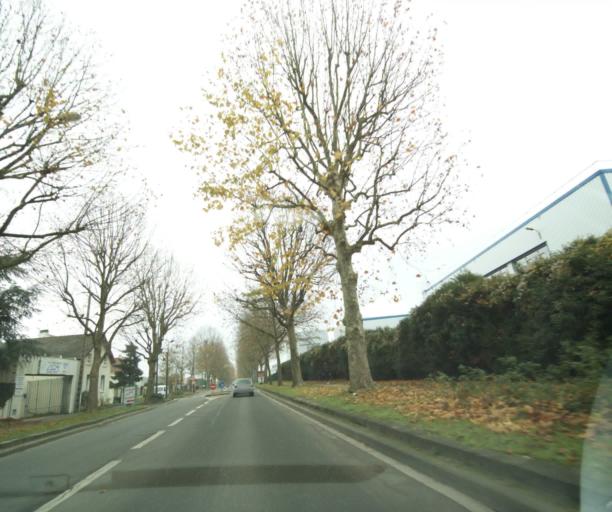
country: FR
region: Ile-de-France
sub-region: Departement de Seine-Saint-Denis
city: Vaujours
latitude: 48.9372
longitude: 2.5899
